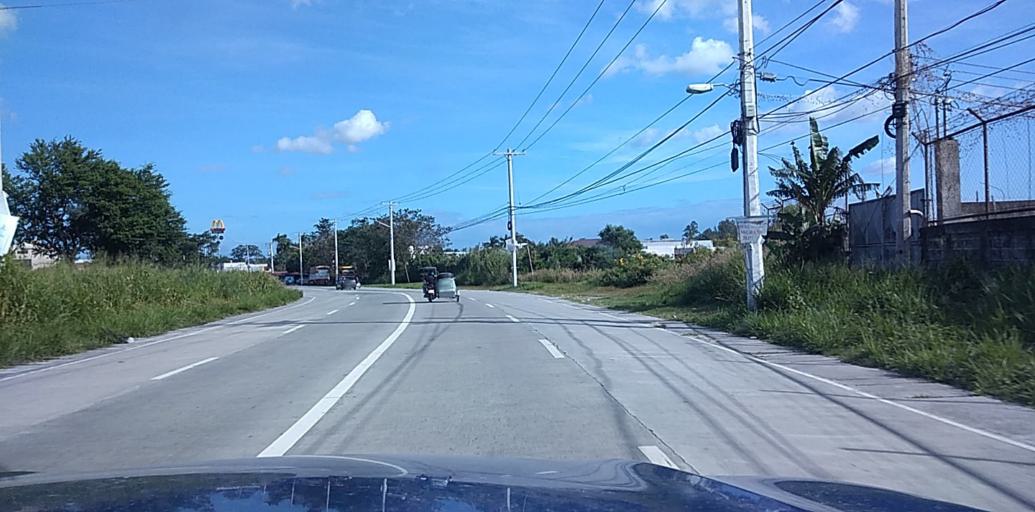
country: PH
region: Central Luzon
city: Santol
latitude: 15.1444
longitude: 120.5565
